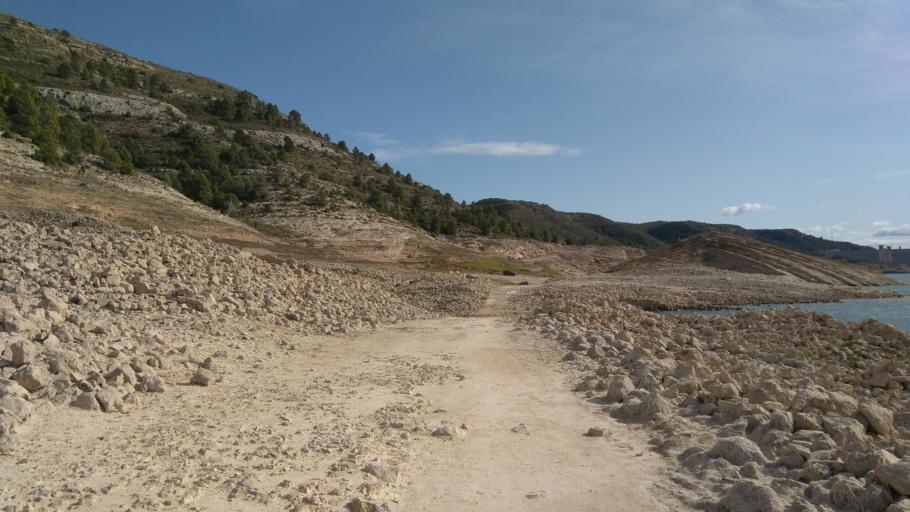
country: ES
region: Valencia
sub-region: Provincia de Valencia
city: Sumacarcer
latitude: 39.1560
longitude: -0.6606
